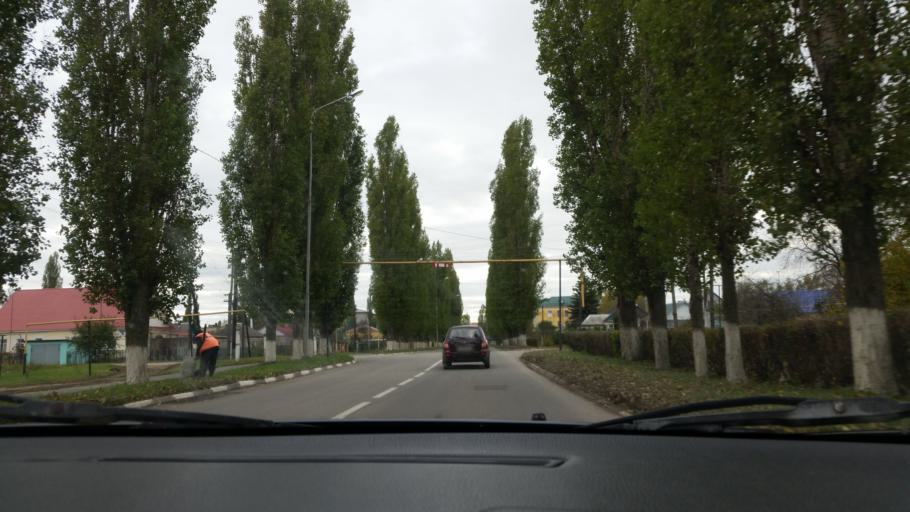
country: RU
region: Lipetsk
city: Gryazi
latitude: 52.4805
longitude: 39.9521
